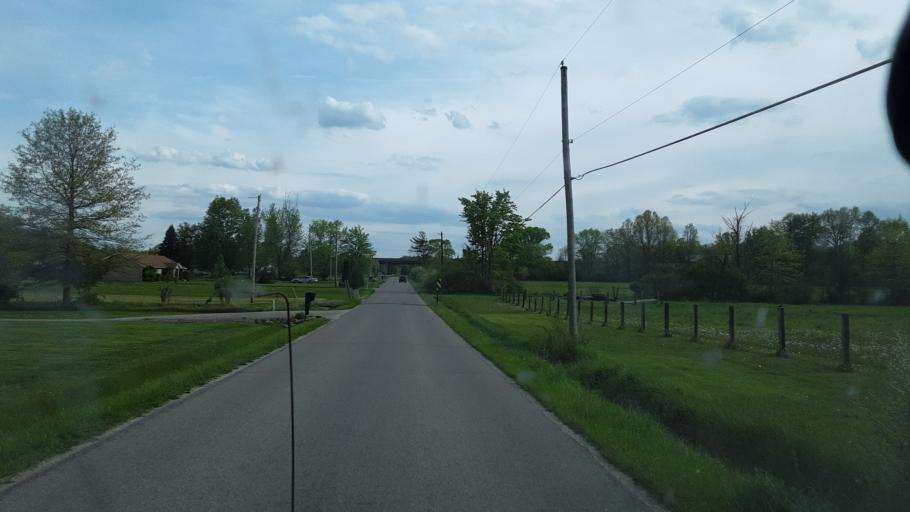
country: US
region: Ohio
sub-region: Portage County
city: Windham
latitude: 41.2455
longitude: -81.0666
